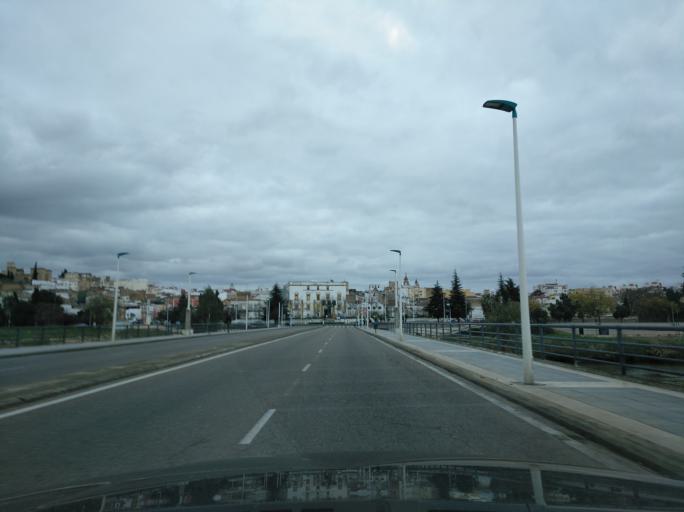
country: ES
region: Extremadura
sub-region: Provincia de Badajoz
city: Badajoz
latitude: 38.8845
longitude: -6.9741
